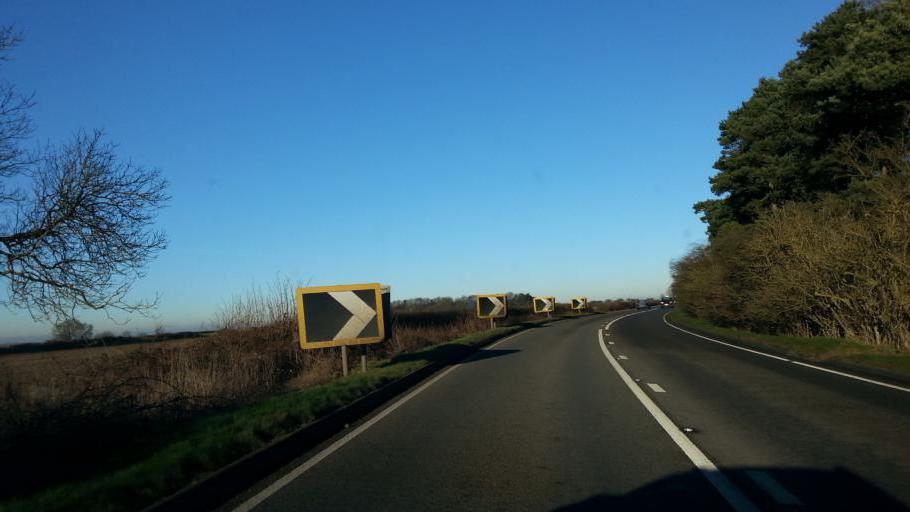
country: GB
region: England
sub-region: Leicestershire
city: Wymondham
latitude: 52.8367
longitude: -0.8030
